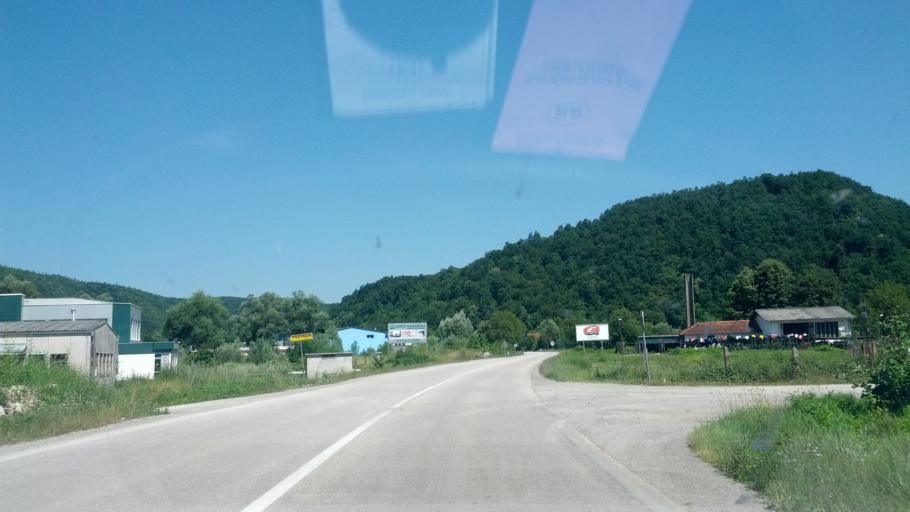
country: BA
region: Federation of Bosnia and Herzegovina
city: Bosanska Krupa
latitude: 44.9095
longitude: 16.1581
